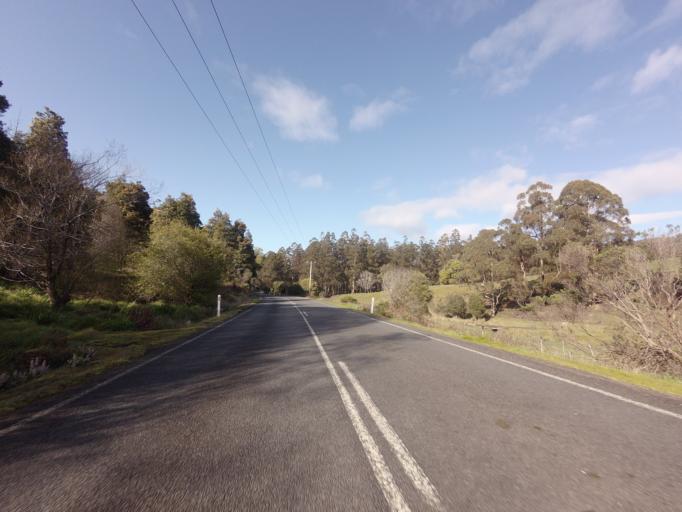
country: AU
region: Tasmania
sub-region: Huon Valley
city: Cygnet
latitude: -43.2703
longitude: 147.0104
